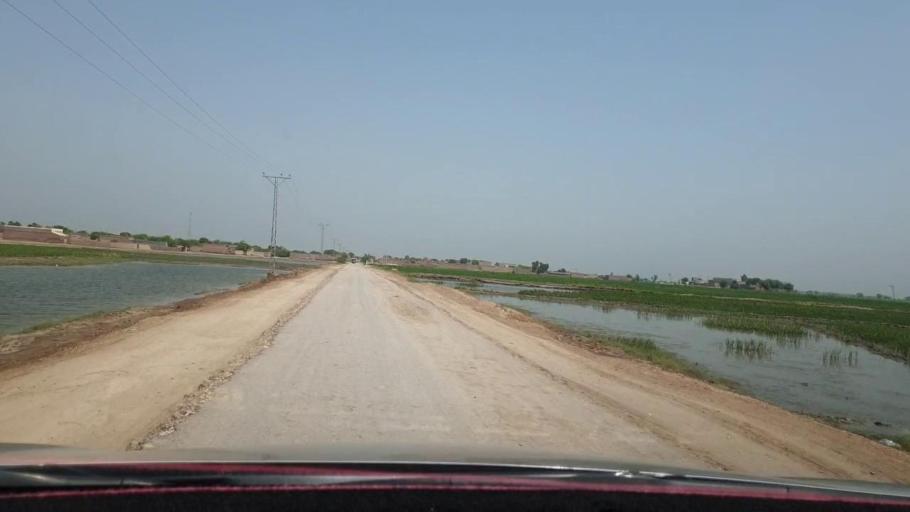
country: PK
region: Sindh
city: Warah
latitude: 27.4415
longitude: 67.7731
